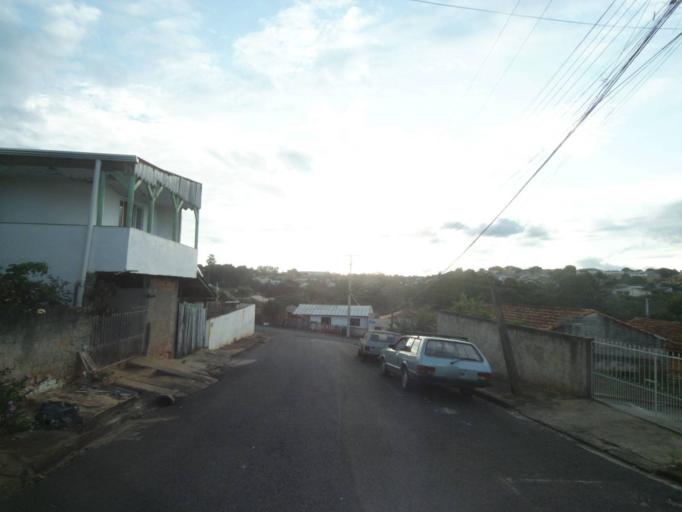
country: BR
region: Parana
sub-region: Telemaco Borba
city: Telemaco Borba
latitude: -24.3248
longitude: -50.6432
